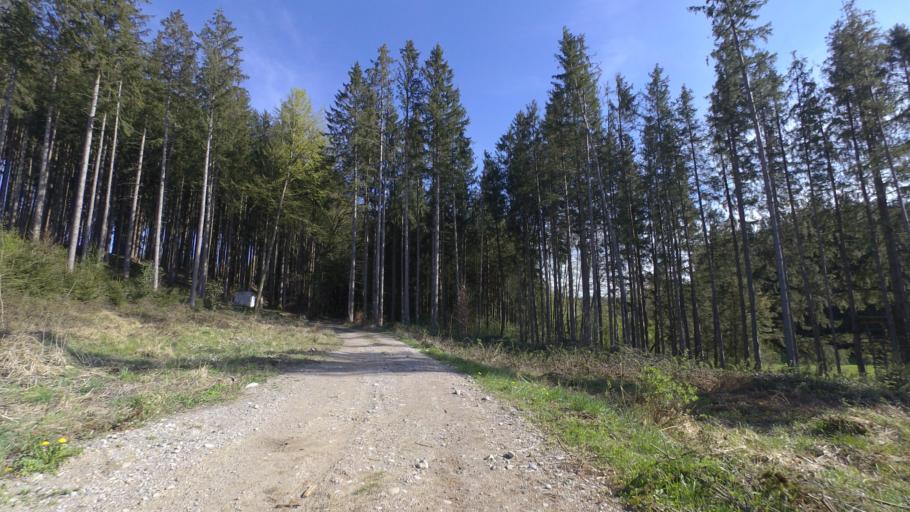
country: DE
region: Bavaria
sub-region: Upper Bavaria
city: Chieming
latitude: 47.8744
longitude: 12.5645
